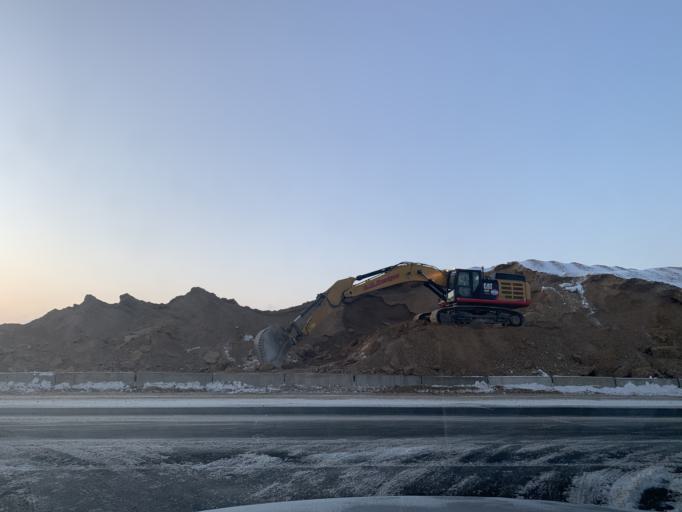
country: US
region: Minnesota
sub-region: Scott County
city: Shakopee
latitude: 44.7938
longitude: -93.4880
